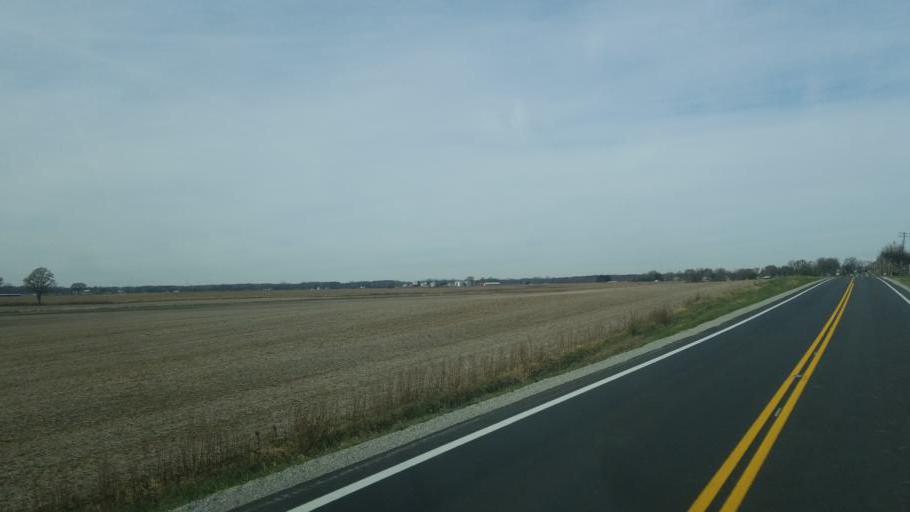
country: US
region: Ohio
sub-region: Madison County
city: Choctaw Lake
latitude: 39.9248
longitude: -83.4866
